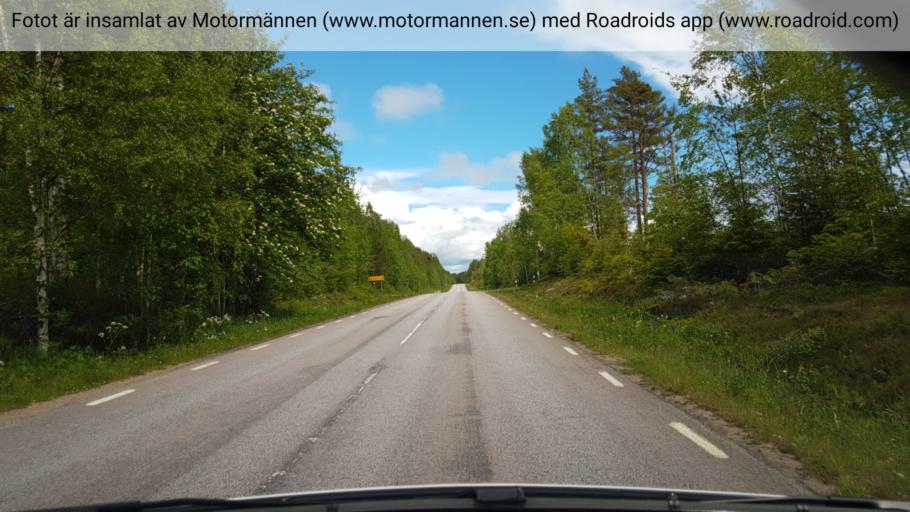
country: SE
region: Vaesterbotten
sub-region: Umea Kommun
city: Hoernefors
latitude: 63.6049
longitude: 19.8590
